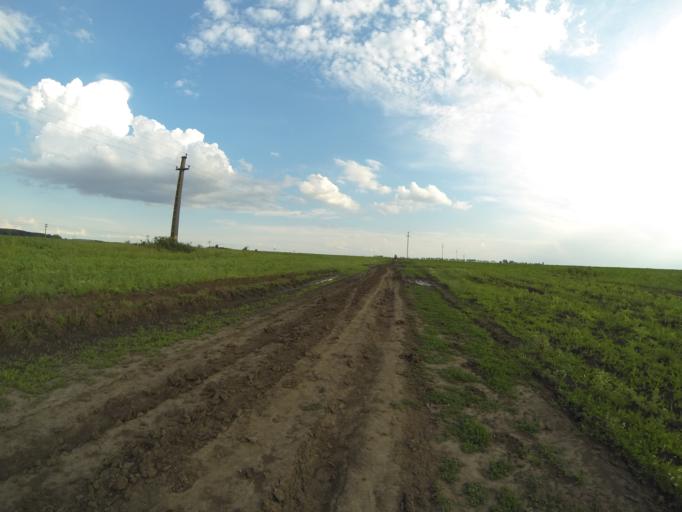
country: RO
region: Dolj
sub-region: Comuna Caloparu
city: Salcuta
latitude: 44.1522
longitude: 23.7039
